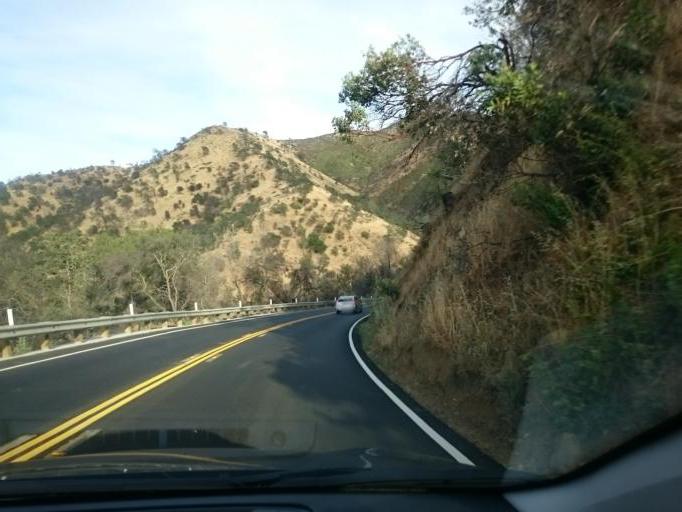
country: US
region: California
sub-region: Yolo County
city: Winters
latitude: 38.5115
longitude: -122.0996
